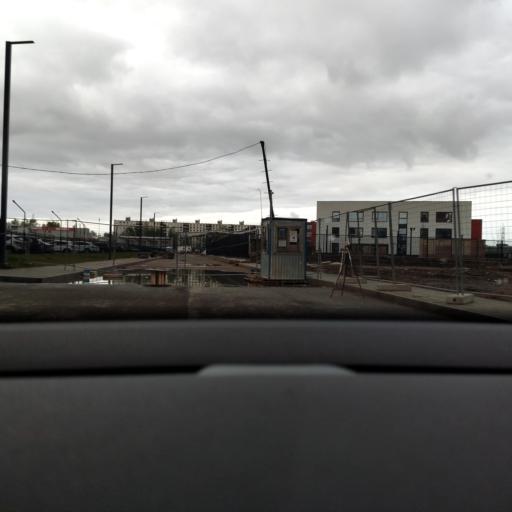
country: RU
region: Moscow
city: Mikhalkovo
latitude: 55.6633
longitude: 37.4203
